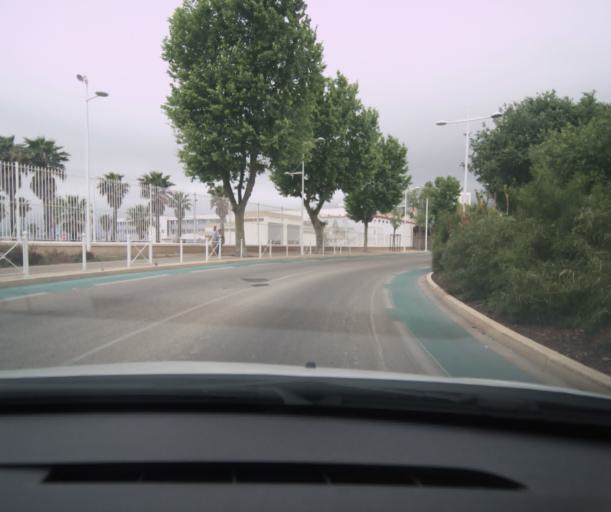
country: FR
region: Provence-Alpes-Cote d'Azur
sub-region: Departement du Var
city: Toulon
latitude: 43.1085
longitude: 5.9309
